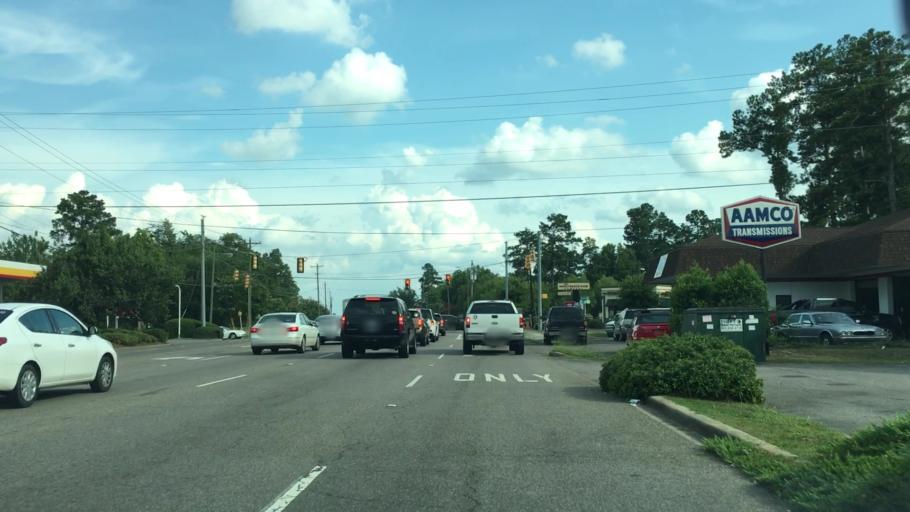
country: US
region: South Carolina
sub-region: Aiken County
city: Aiken
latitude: 33.5312
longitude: -81.7240
